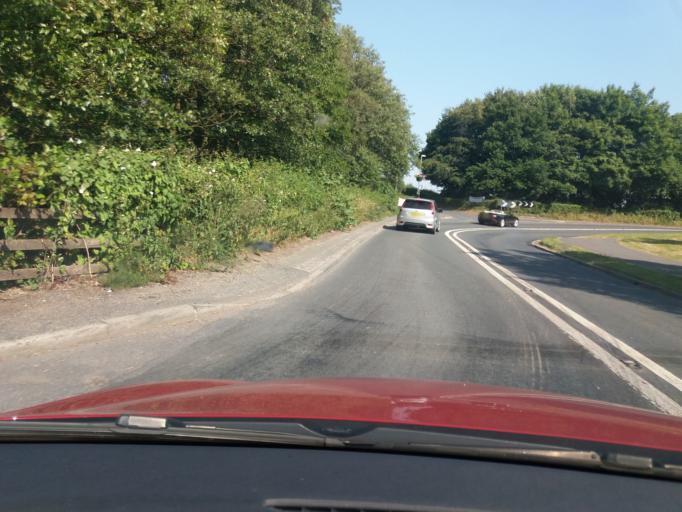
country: GB
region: England
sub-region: Lancashire
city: Clayton-le-Woods
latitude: 53.6875
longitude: -2.6565
